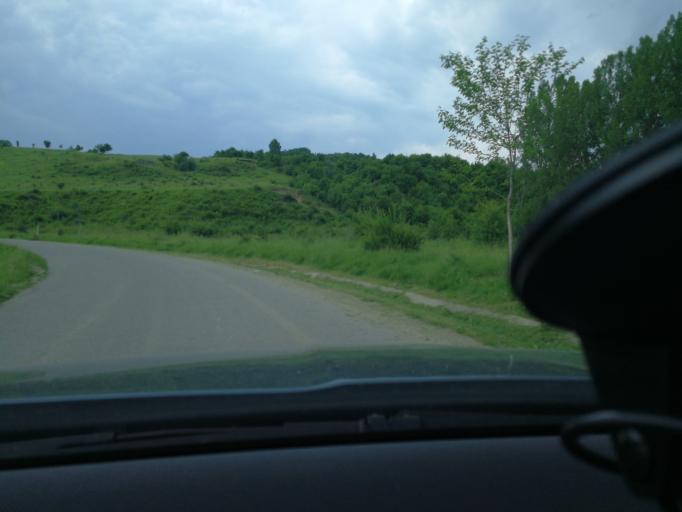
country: RO
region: Prahova
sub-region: Comuna Cornu
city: Cornu de Jos
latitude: 45.1479
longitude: 25.7258
